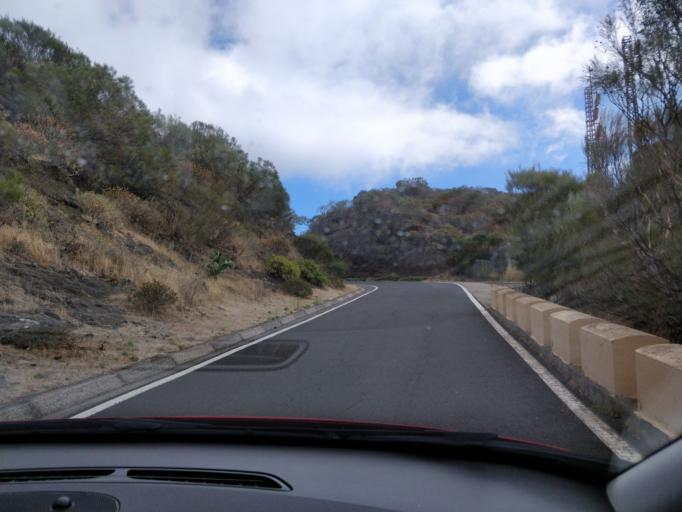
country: ES
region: Canary Islands
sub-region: Provincia de Santa Cruz de Tenerife
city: Santiago del Teide
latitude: 28.3167
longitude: -16.8524
